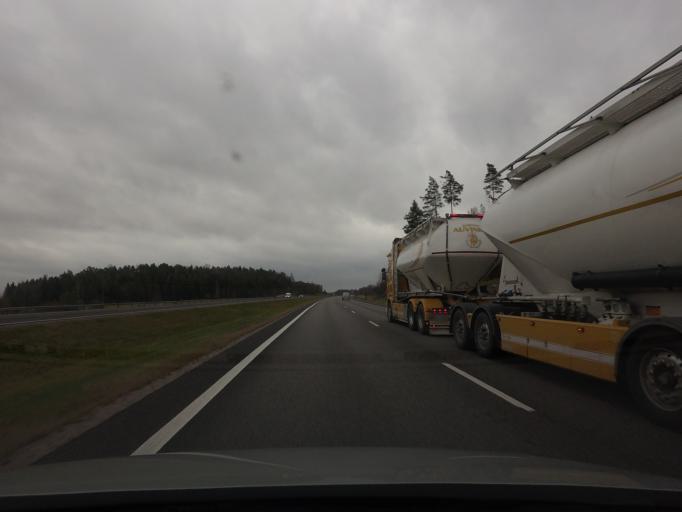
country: FI
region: Varsinais-Suomi
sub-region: Turku
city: Paimio
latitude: 60.4404
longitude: 22.6211
